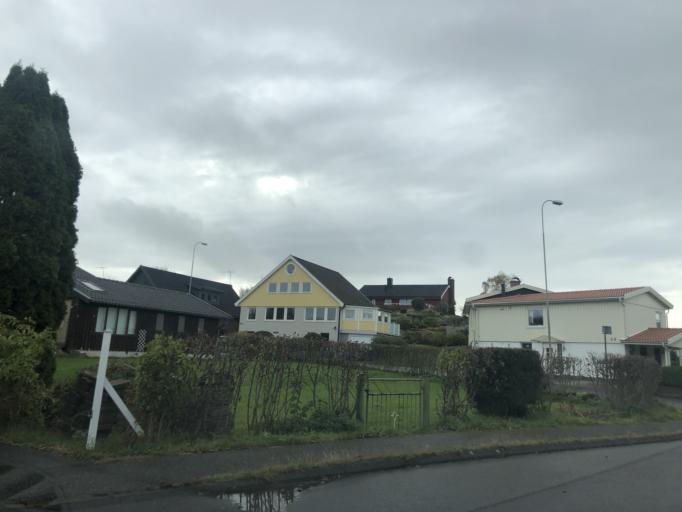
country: SE
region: Vaestra Goetaland
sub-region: Goteborg
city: Majorna
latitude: 57.6687
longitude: 11.9016
